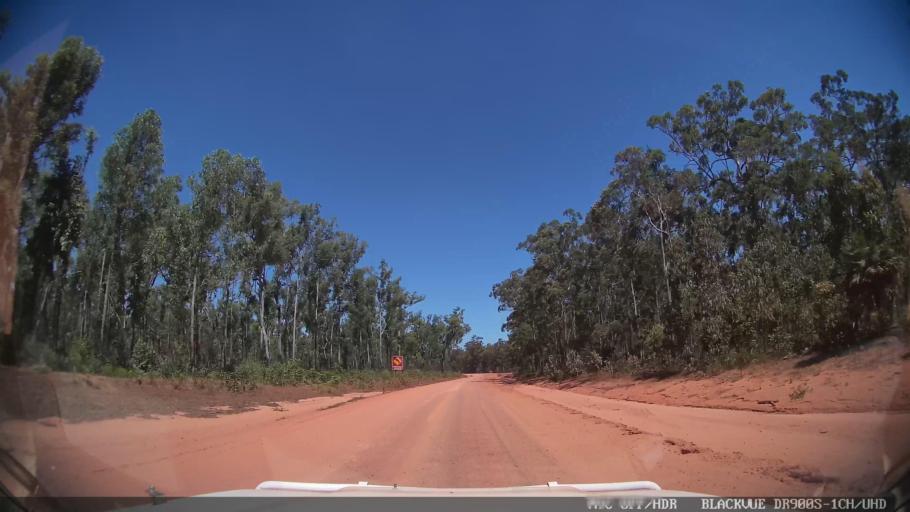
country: AU
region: Queensland
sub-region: Torres
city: Thursday Island
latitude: -11.1853
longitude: 142.2545
